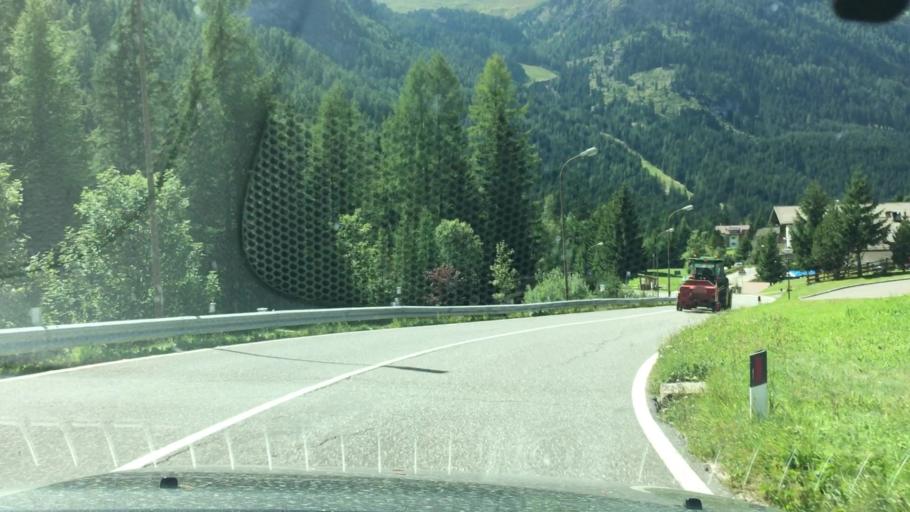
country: IT
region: Trentino-Alto Adige
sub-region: Provincia di Trento
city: Canazei
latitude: 46.4571
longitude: 11.8036
